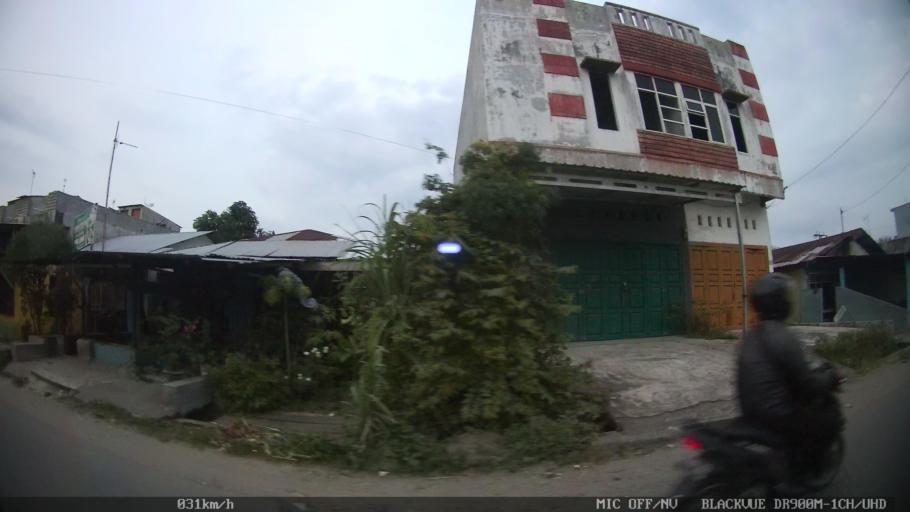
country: ID
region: North Sumatra
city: Sunggal
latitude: 3.5923
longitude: 98.6025
